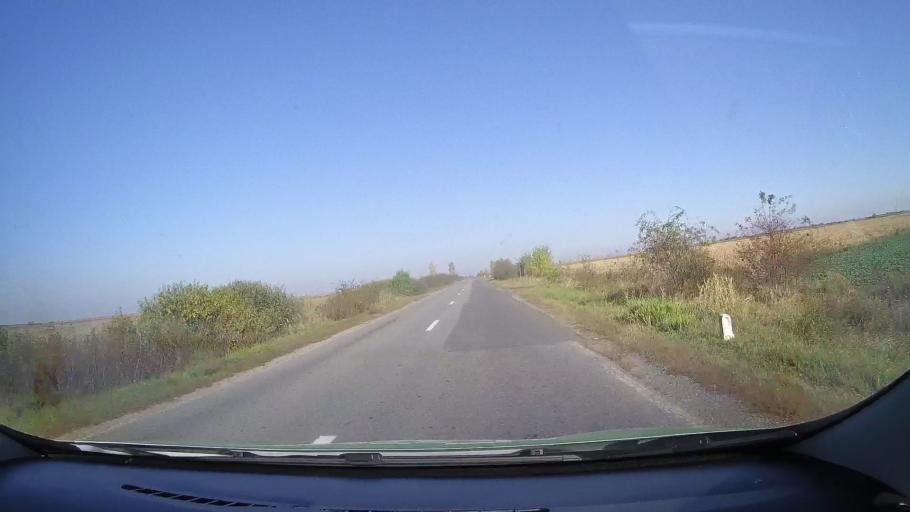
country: RO
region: Satu Mare
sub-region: Oras Tasnad
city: Tasnad
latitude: 47.5256
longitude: 22.5686
